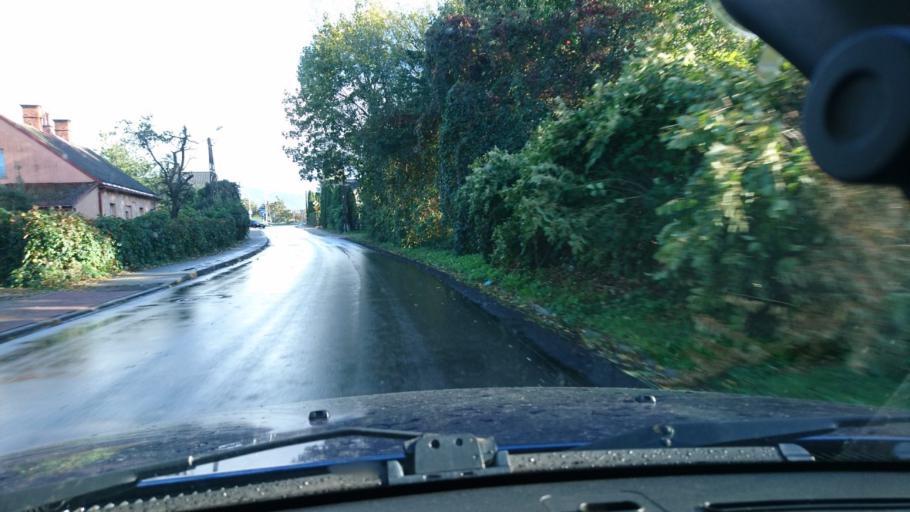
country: PL
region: Silesian Voivodeship
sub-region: Bielsko-Biala
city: Bielsko-Biala
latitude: 49.8463
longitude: 19.0478
